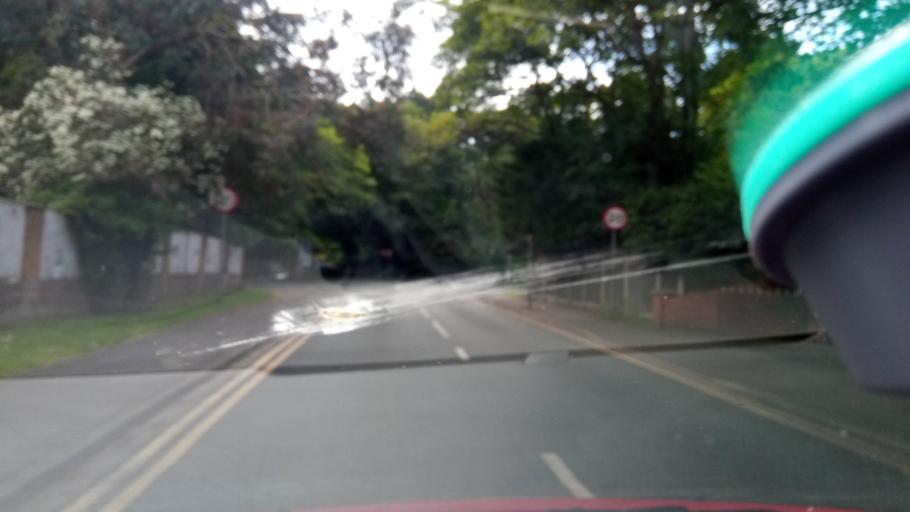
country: GB
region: England
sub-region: Sefton
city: Formby
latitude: 53.5510
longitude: -3.0859
